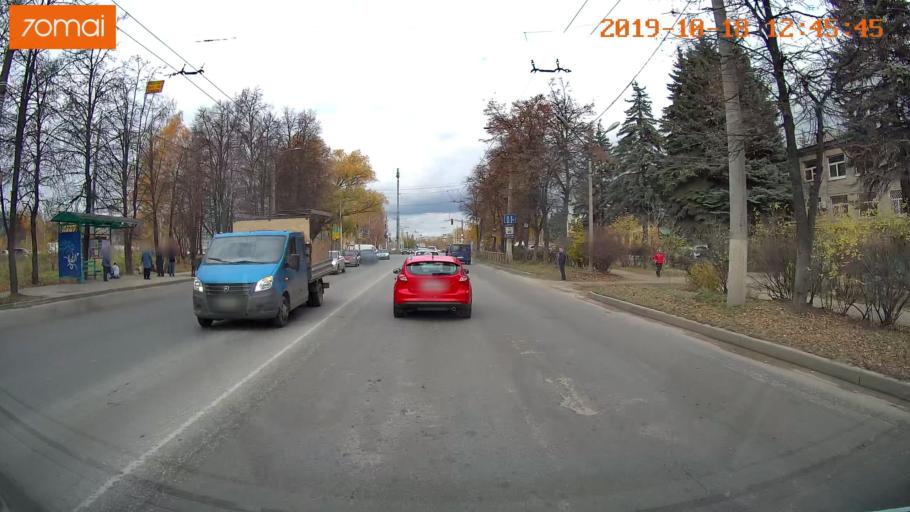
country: RU
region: Rjazan
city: Ryazan'
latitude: 54.6540
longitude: 39.6653
